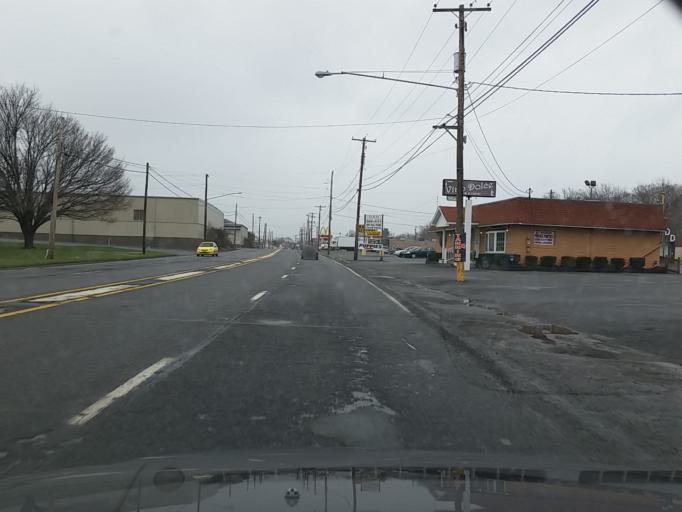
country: US
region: Pennsylvania
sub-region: Luzerne County
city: Larksville
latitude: 41.2302
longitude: -75.9245
